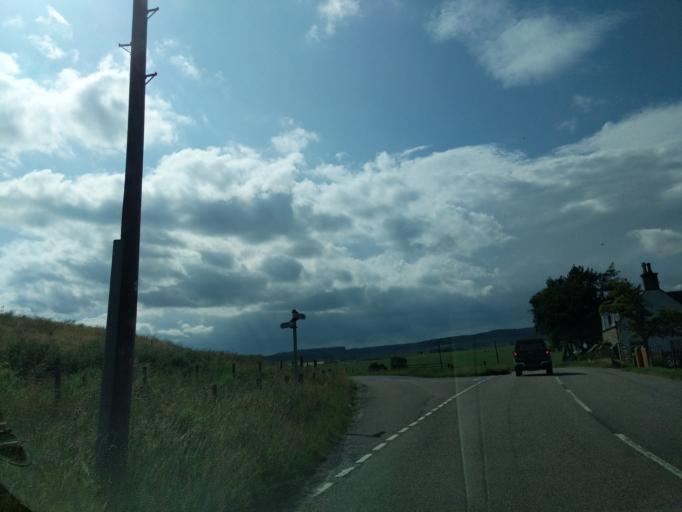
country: GB
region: Scotland
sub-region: Moray
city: Rothes
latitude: 57.4914
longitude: -3.2166
